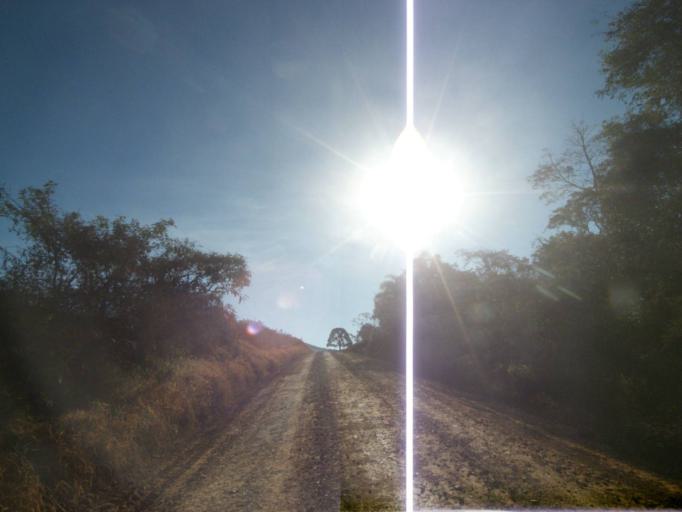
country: BR
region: Parana
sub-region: Tibagi
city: Tibagi
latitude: -24.5251
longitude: -50.4954
